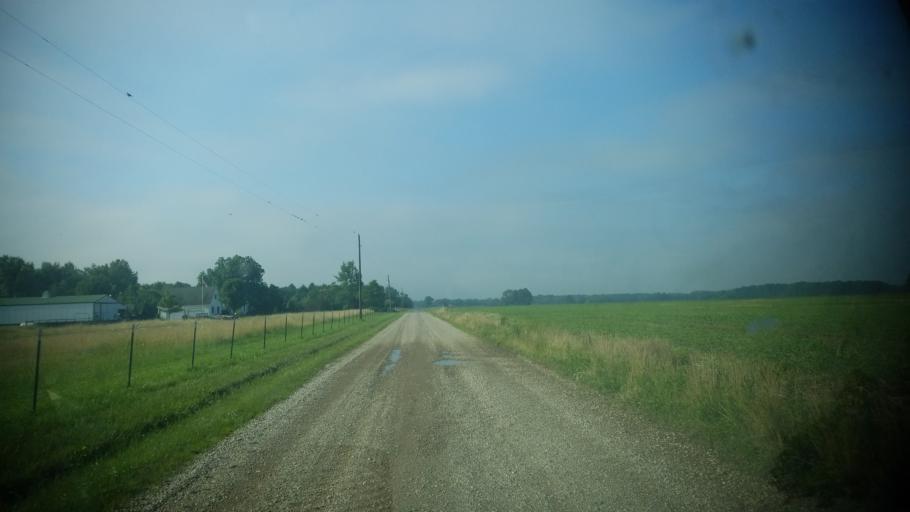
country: US
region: Illinois
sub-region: Clay County
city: Flora
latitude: 38.5969
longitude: -88.3643
